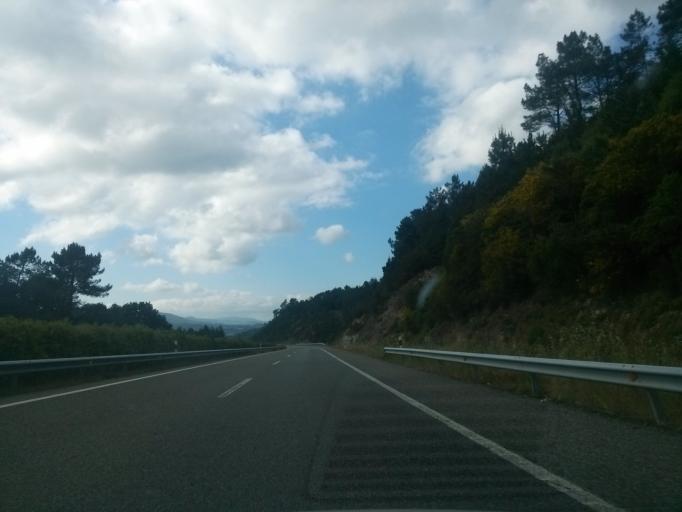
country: ES
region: Galicia
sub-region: Provincia de Lugo
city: Becerrea
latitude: 42.8972
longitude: -7.1868
